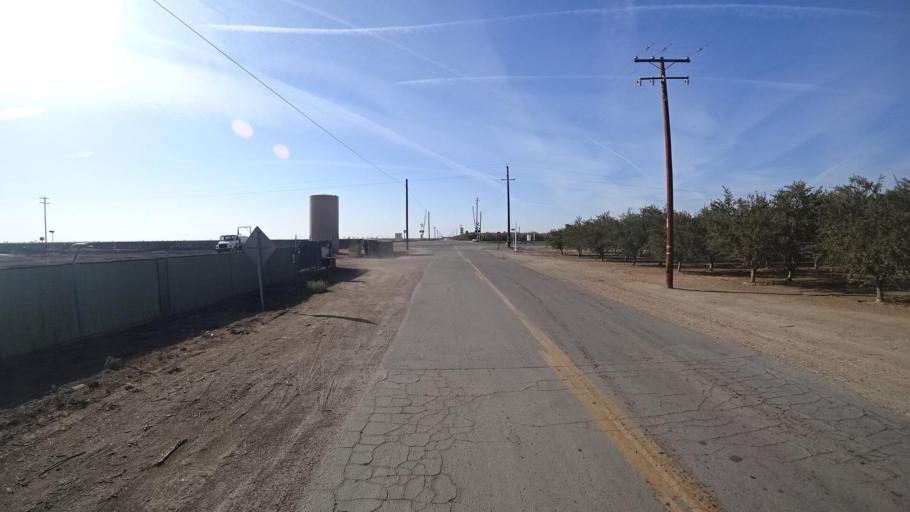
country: US
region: California
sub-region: Kern County
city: McFarland
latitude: 35.7027
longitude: -119.3297
